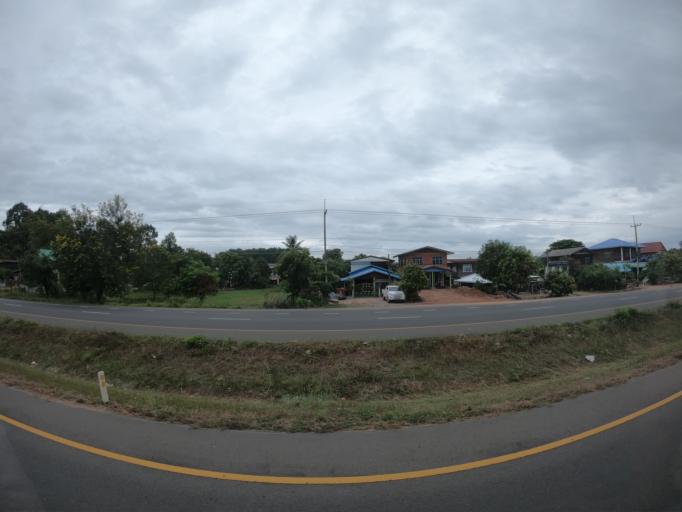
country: TH
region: Kalasin
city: Khong Chai
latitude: 16.1388
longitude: 103.4356
